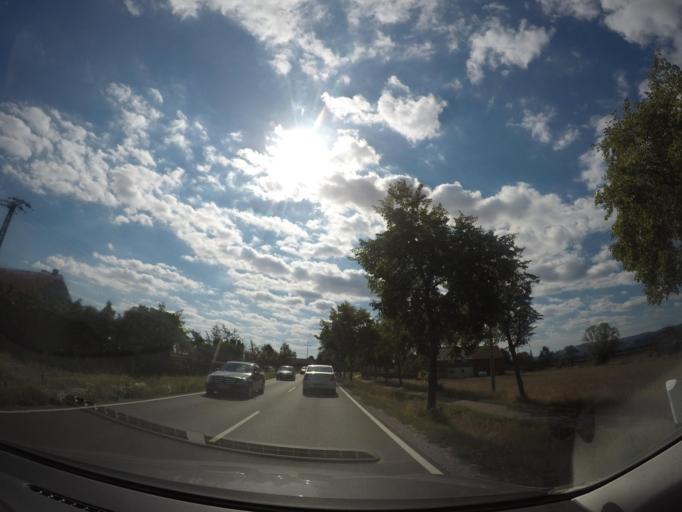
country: DE
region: Saxony-Anhalt
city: Langeln
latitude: 51.8867
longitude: 10.7690
